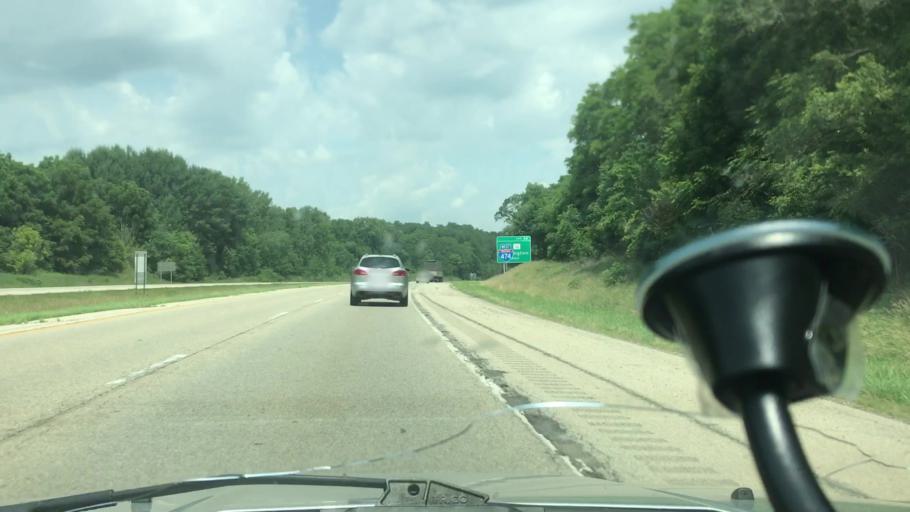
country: US
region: Illinois
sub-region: Peoria County
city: Bellevue
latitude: 40.6744
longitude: -89.6714
